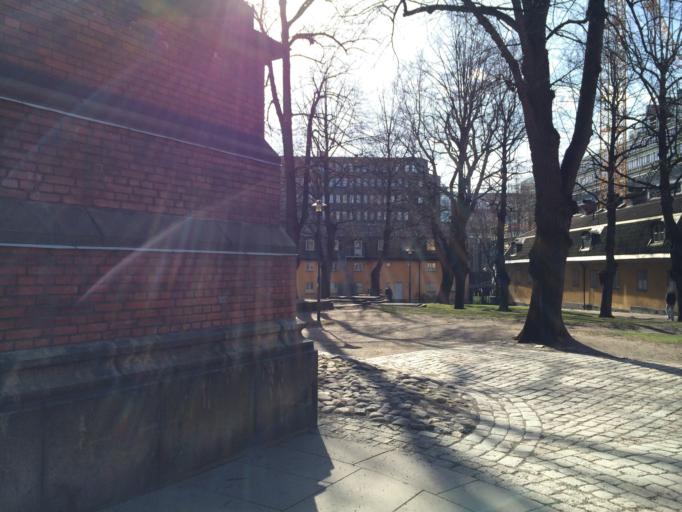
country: SE
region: Stockholm
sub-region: Stockholms Kommun
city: Stockholm
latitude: 59.3313
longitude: 18.0610
